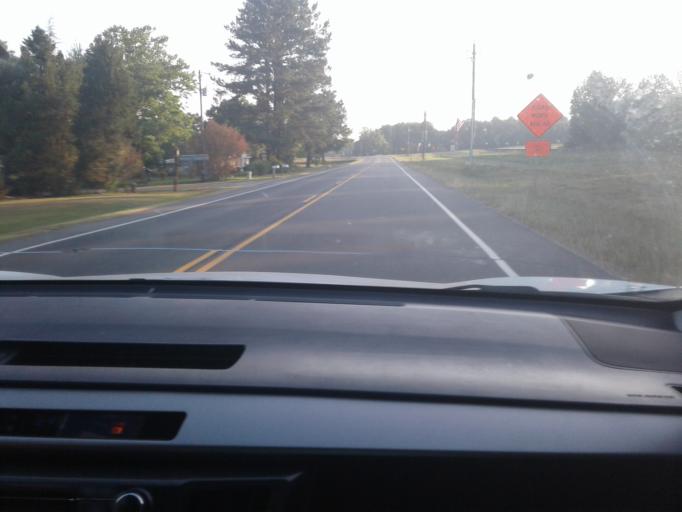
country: US
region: North Carolina
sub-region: Harnett County
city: Angier
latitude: 35.4880
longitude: -78.8168
